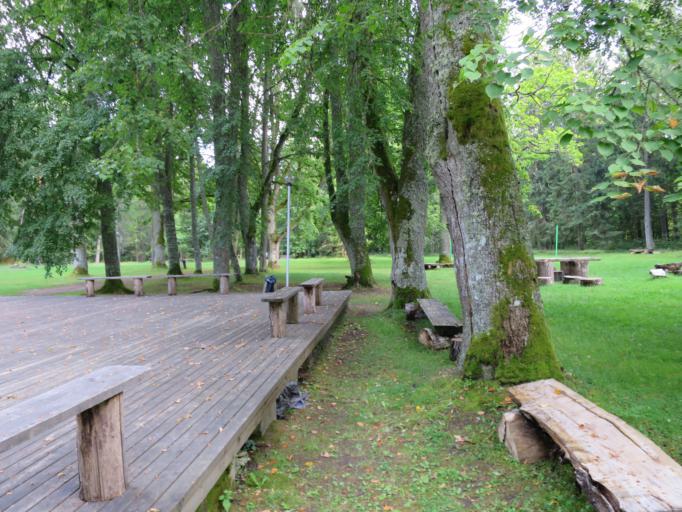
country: LV
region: Priekuli
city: Priekuli
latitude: 57.2867
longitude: 25.4669
